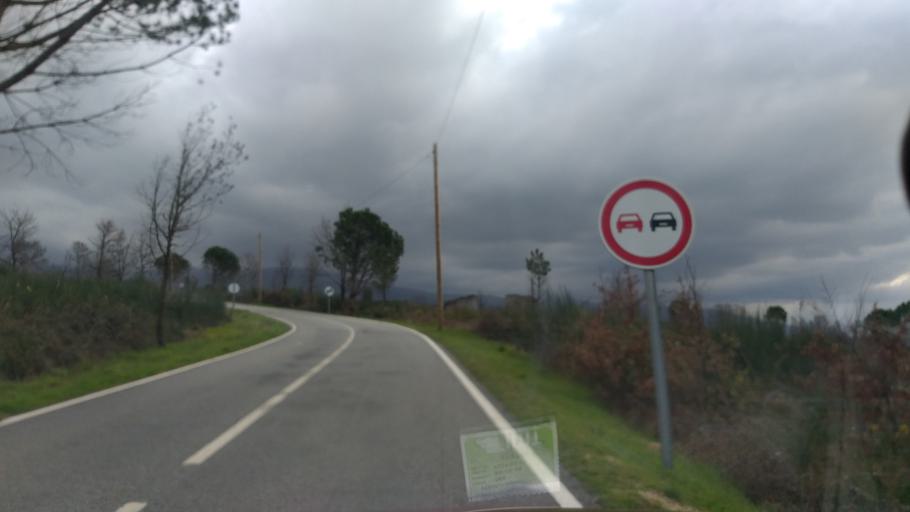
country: PT
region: Guarda
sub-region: Seia
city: Seia
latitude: 40.4834
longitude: -7.6539
